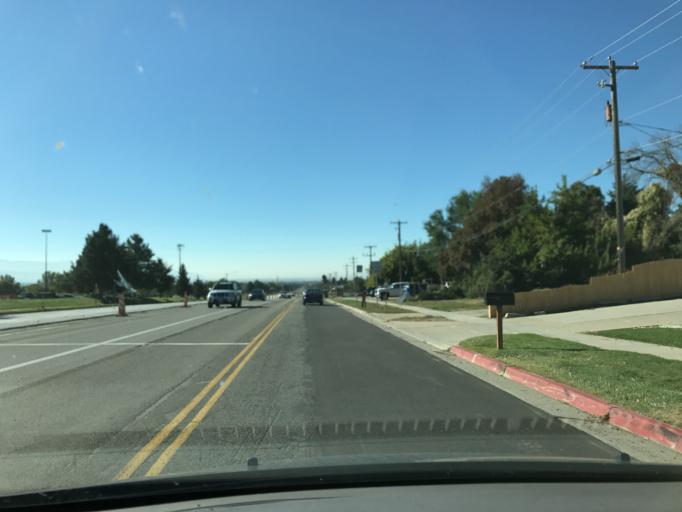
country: US
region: Utah
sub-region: Davis County
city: Hill Air Force Bace
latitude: 41.0960
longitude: -111.9735
